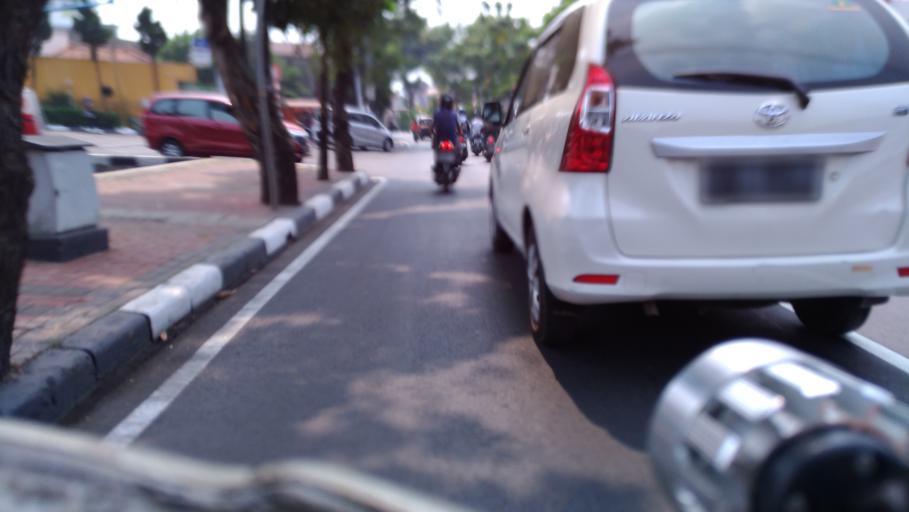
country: ID
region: West Java
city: Cileungsir
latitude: -6.3168
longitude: 106.8918
